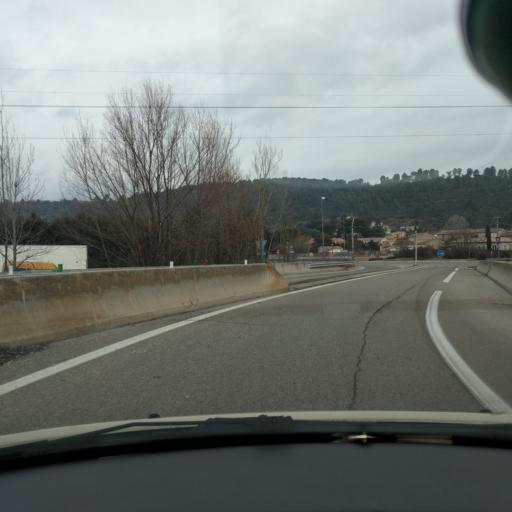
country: FR
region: Provence-Alpes-Cote d'Azur
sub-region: Departement des Bouches-du-Rhone
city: Meyreuil
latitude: 43.4746
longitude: 5.5163
